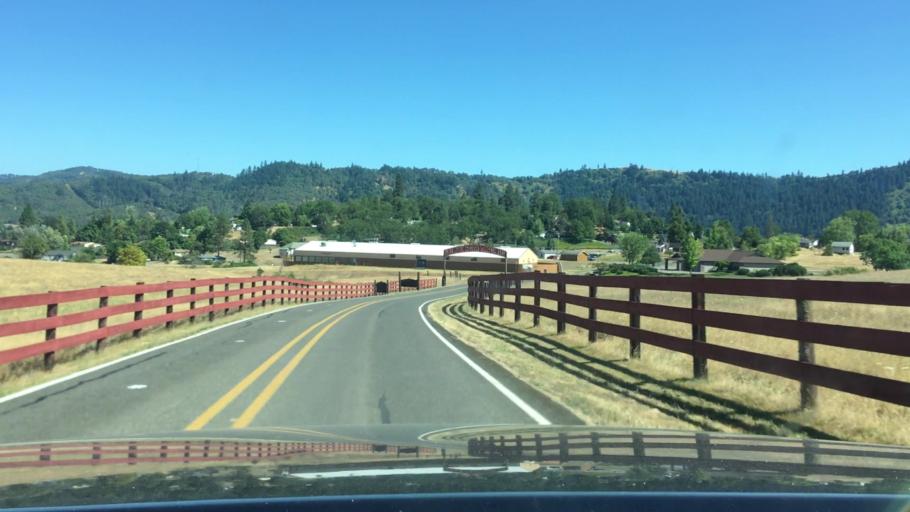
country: US
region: Oregon
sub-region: Douglas County
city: Winston
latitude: 43.1300
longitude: -123.4138
